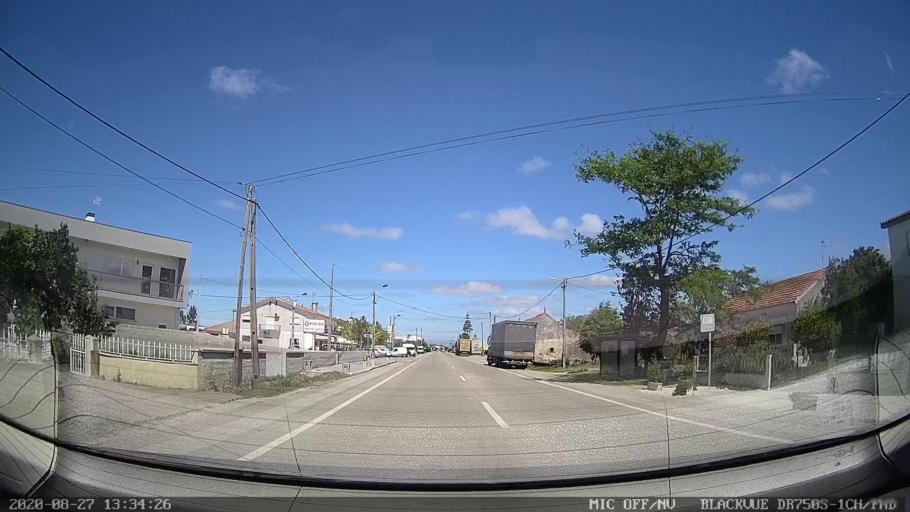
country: PT
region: Coimbra
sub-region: Mira
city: Mira
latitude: 40.4716
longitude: -8.6974
